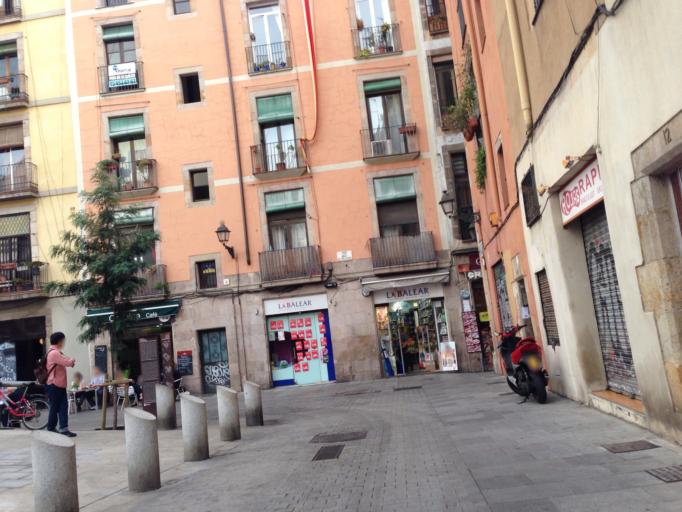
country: ES
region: Catalonia
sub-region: Provincia de Barcelona
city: Ciutat Vella
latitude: 41.3859
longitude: 2.1792
